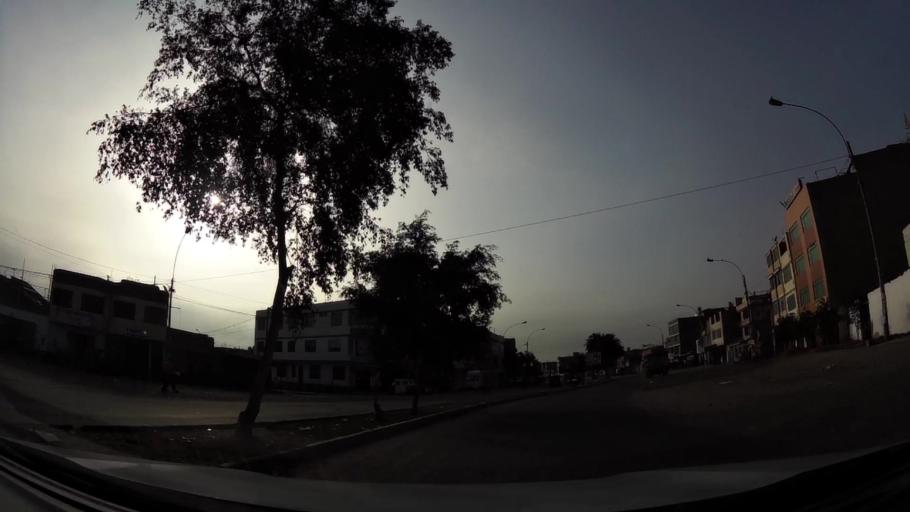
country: PE
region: Lima
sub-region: Lima
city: Independencia
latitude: -11.9951
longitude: -77.1049
